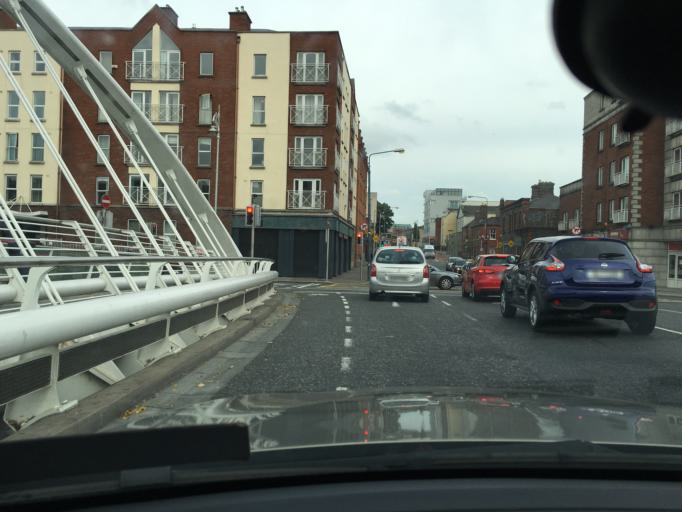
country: IE
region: Leinster
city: Rialto
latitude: 53.3466
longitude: -6.2827
